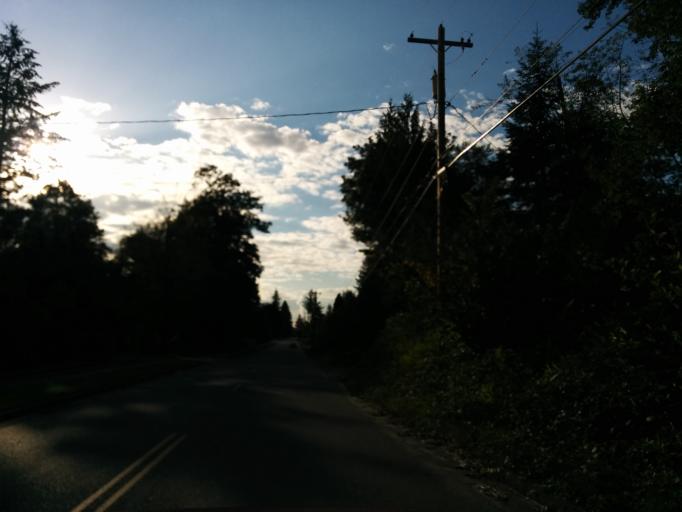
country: US
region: Washington
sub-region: Snohomish County
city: Gold Bar
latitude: 47.8598
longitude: -121.6879
